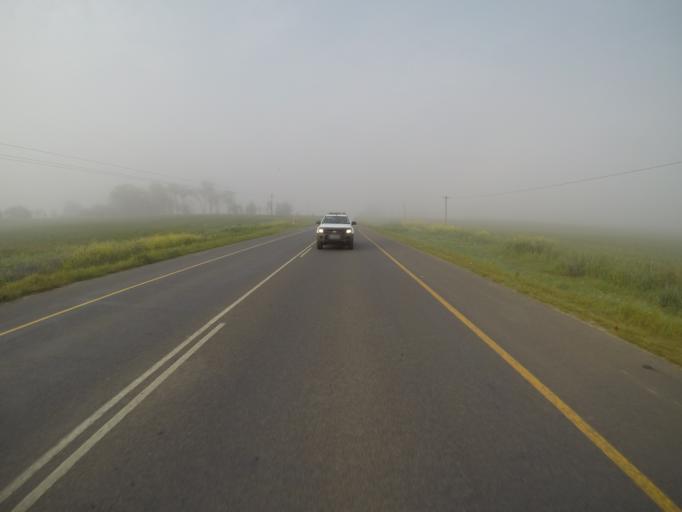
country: ZA
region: Western Cape
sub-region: City of Cape Town
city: Kraaifontein
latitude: -33.7775
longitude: 18.7071
